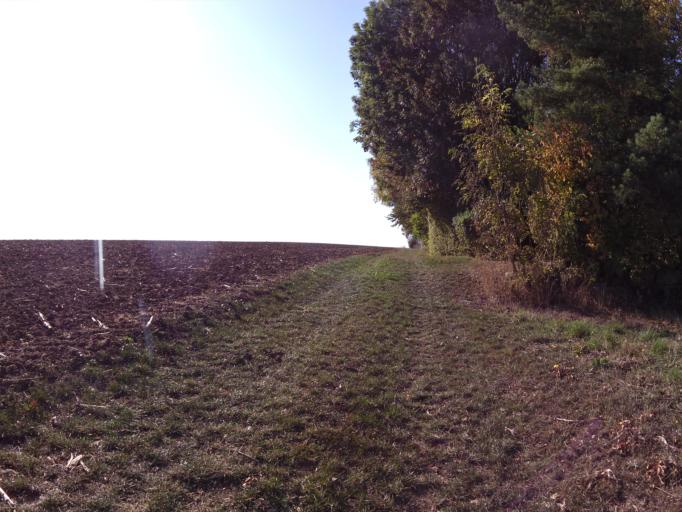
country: DE
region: Bavaria
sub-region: Regierungsbezirk Unterfranken
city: Geroldshausen
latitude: 49.6953
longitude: 9.9207
